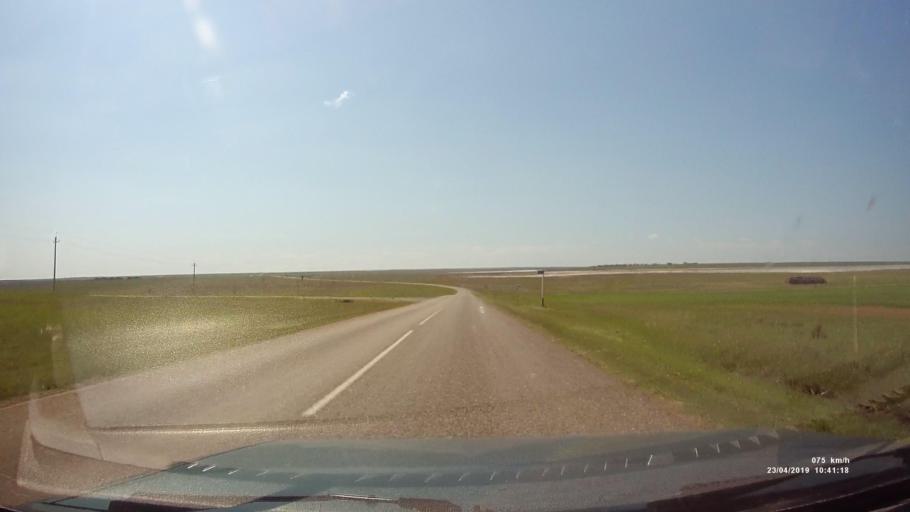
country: RU
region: Kalmykiya
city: Yashalta
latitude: 46.4955
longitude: 42.6381
